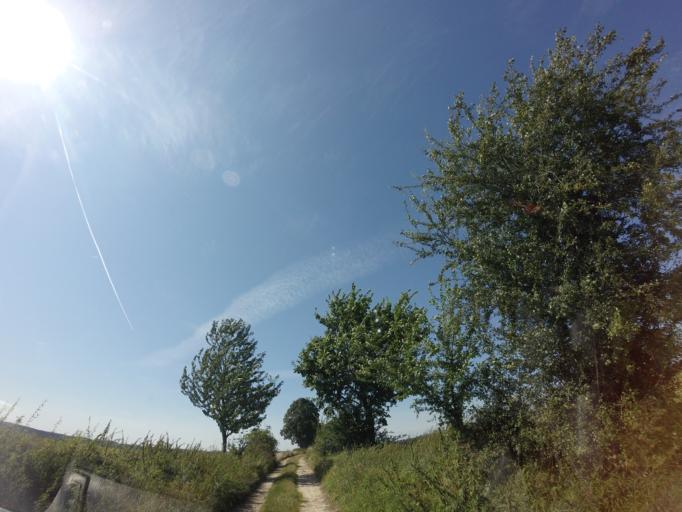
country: PL
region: West Pomeranian Voivodeship
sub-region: Powiat choszczenski
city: Choszczno
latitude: 53.1786
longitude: 15.3814
